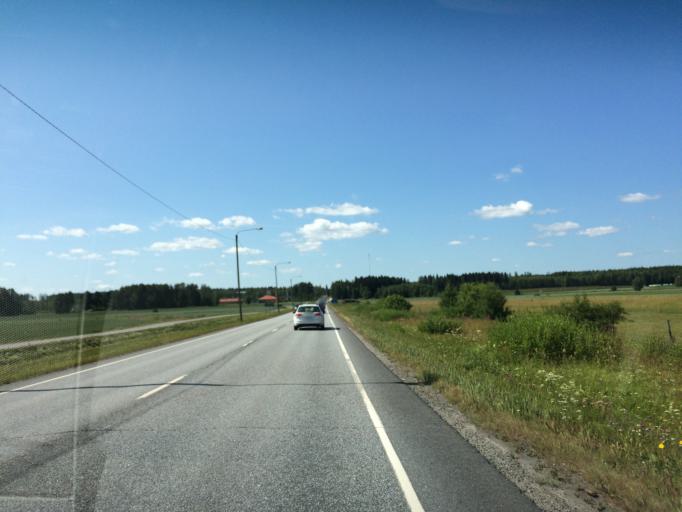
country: FI
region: Pirkanmaa
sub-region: Lounais-Pirkanmaa
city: Kiikoinen
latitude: 61.4762
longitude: 22.5706
